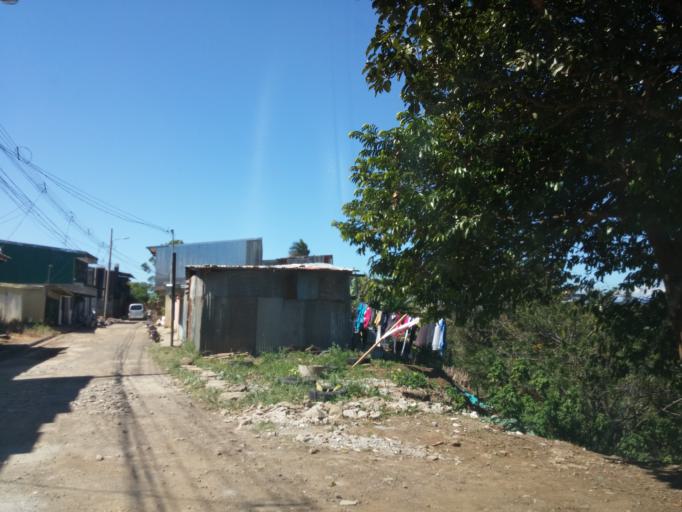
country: CR
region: San Jose
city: Colima
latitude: 9.9436
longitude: -84.0913
